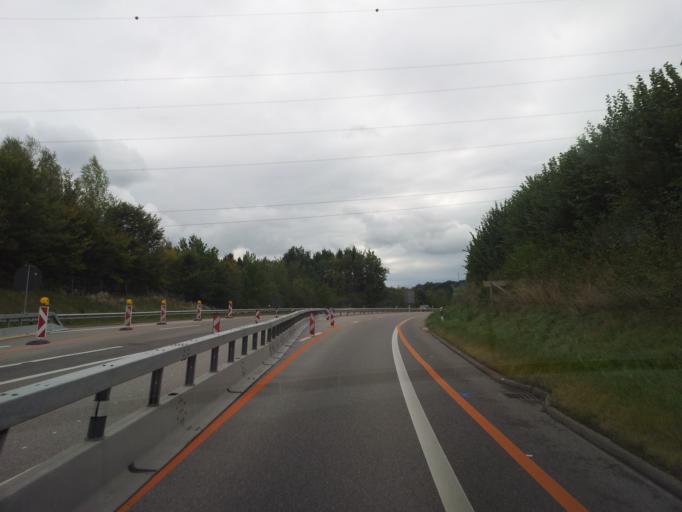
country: CH
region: Fribourg
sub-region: See District
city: Kerzers
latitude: 46.9658
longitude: 7.1934
